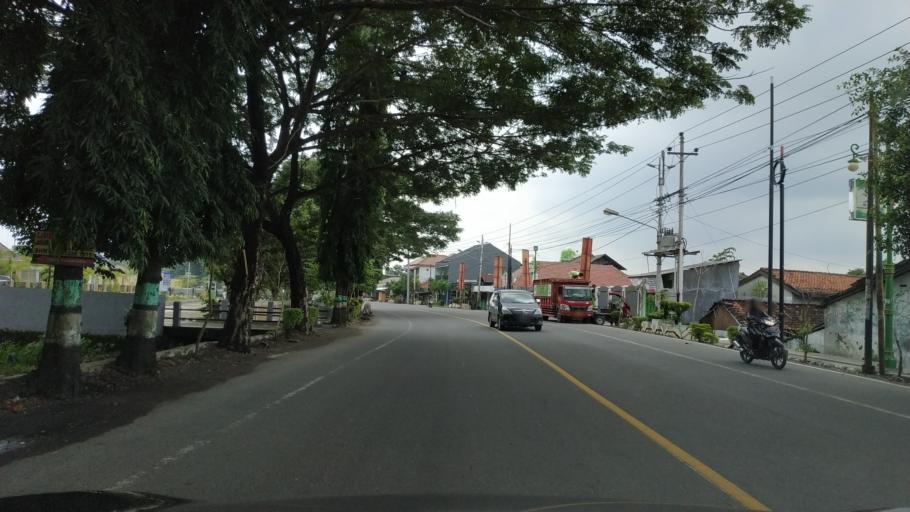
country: ID
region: Central Java
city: Slawi
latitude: -6.9976
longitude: 109.1411
